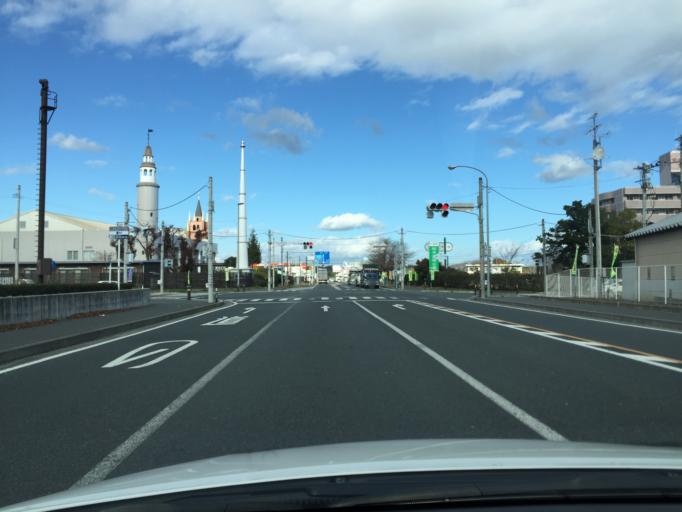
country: JP
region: Fukushima
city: Namie
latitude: 37.6359
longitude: 140.9843
